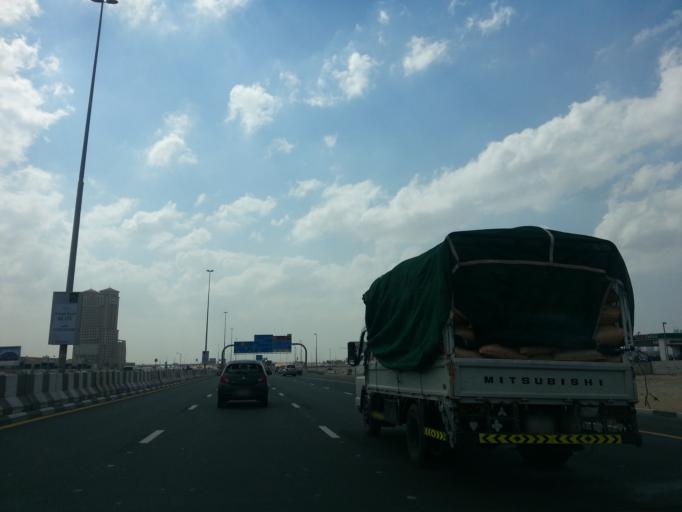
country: AE
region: Ash Shariqah
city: Sharjah
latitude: 25.2196
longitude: 55.3147
